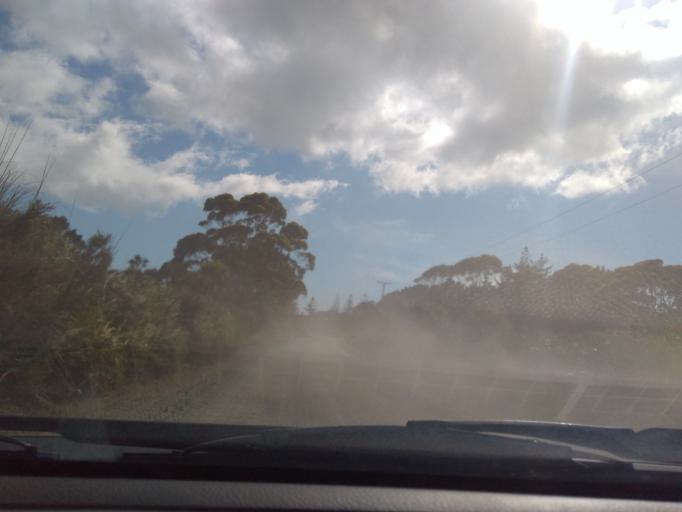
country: NZ
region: Northland
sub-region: Far North District
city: Taipa
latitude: -34.9457
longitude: 173.3802
